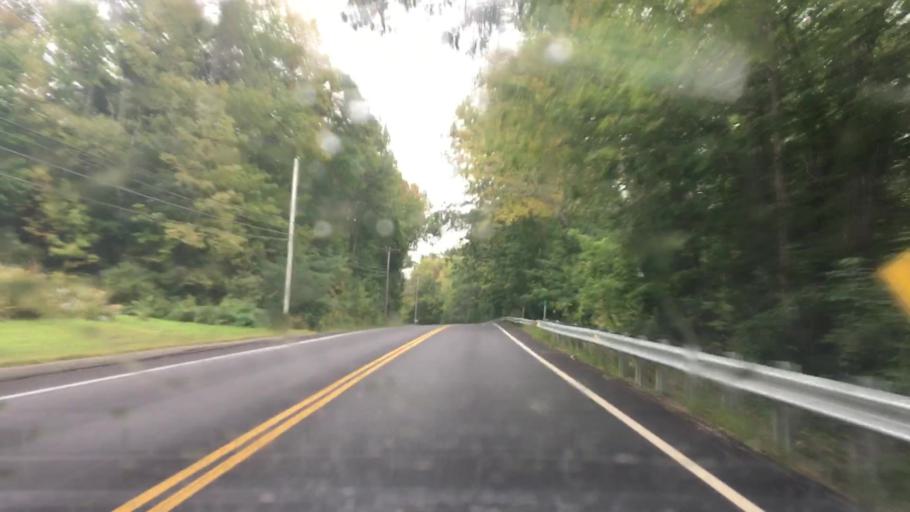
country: US
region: Maine
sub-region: Penobscot County
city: Orrington
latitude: 44.6807
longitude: -68.8082
